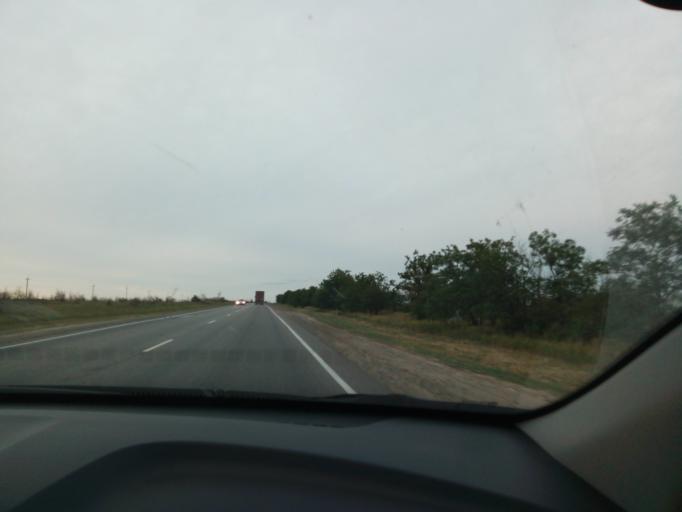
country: RU
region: Volgograd
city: Dubovka
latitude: 49.1419
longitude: 44.8282
